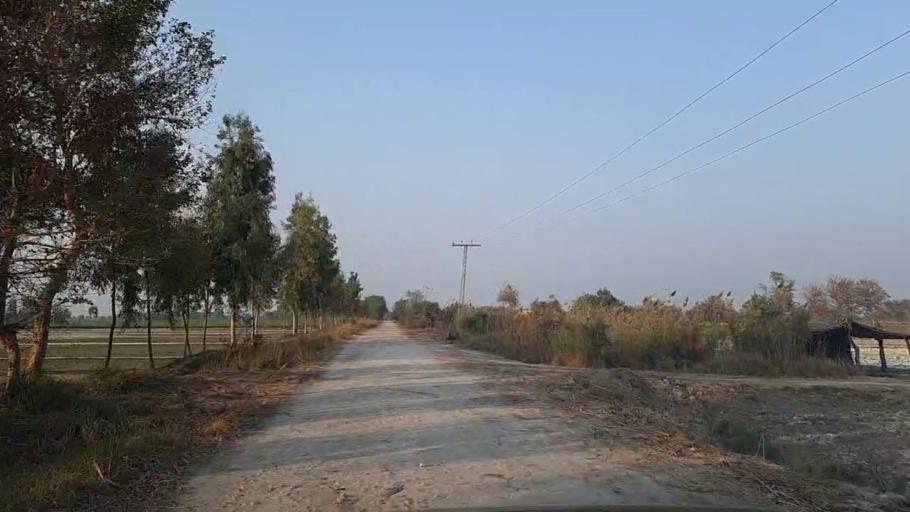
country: PK
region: Sindh
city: Daur
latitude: 26.4287
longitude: 68.3937
